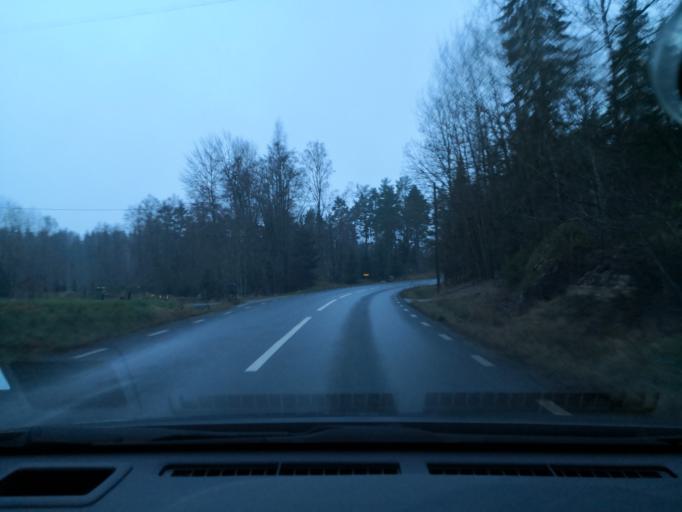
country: SE
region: Soedermanland
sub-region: Katrineholms Kommun
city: Katrineholm
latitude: 59.2017
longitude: 16.2659
